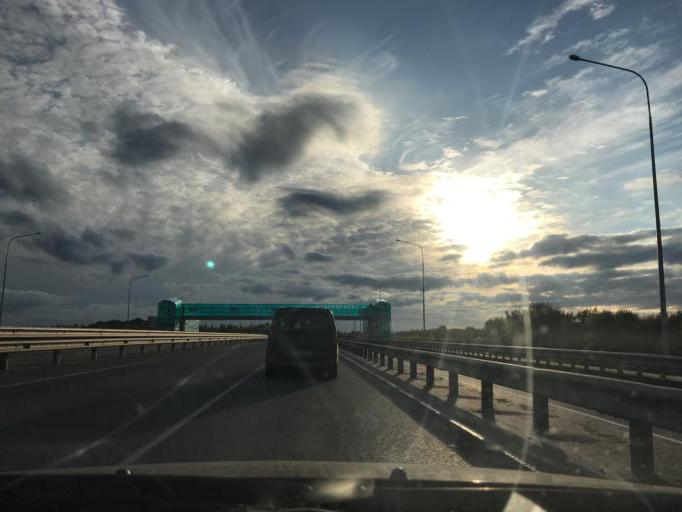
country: RU
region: Kaluga
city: Kurovskoye
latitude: 54.5406
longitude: 36.0067
